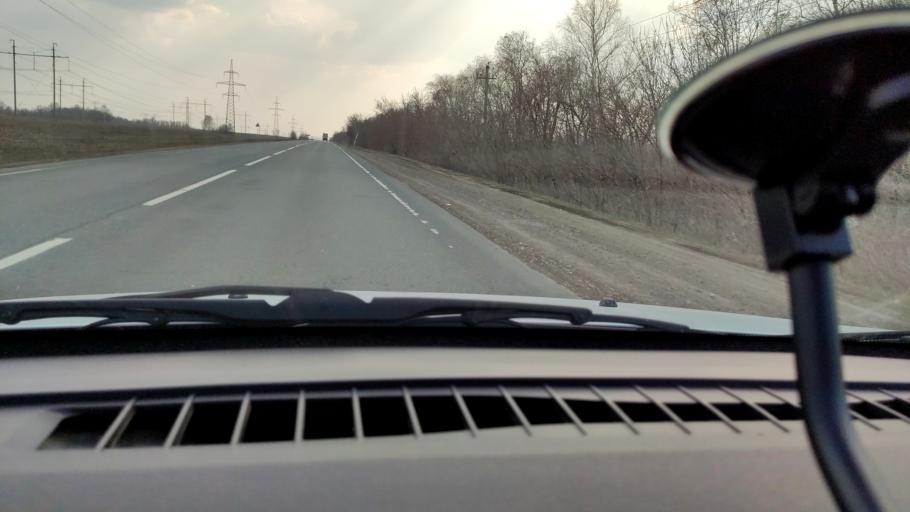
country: RU
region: Samara
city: Dubovyy Umet
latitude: 53.0771
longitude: 50.3871
